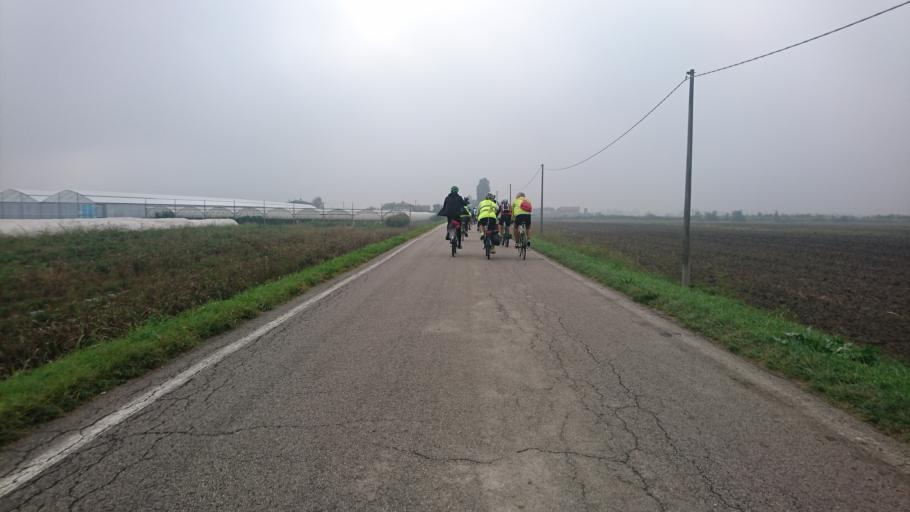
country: IT
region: Veneto
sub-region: Provincia di Padova
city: Pozzonovo
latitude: 45.1665
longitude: 11.7880
